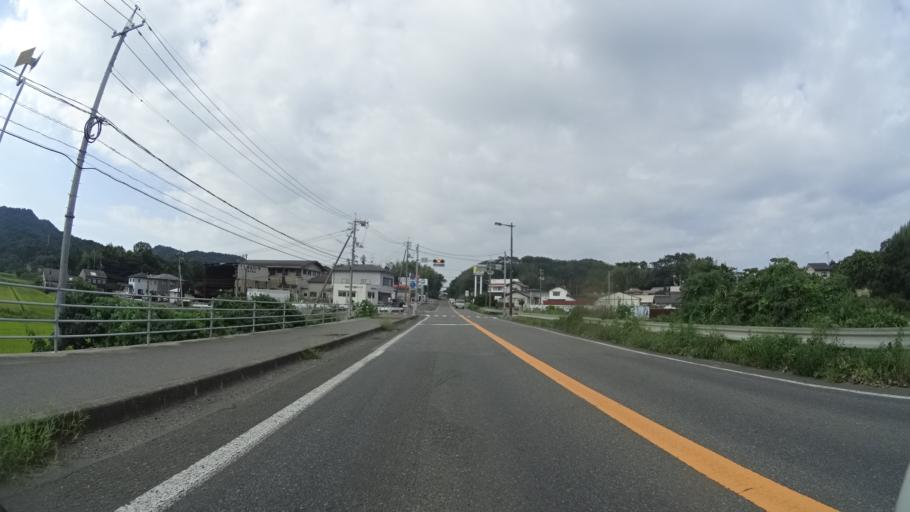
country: JP
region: Shimane
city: Odacho-oda
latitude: 35.2217
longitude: 132.5131
